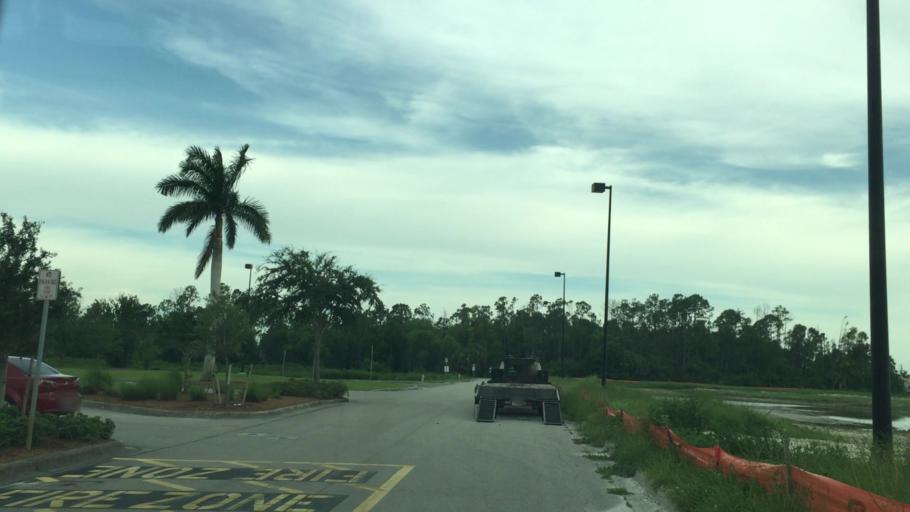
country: US
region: Florida
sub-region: Lee County
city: Fort Myers
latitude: 26.6034
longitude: -81.8100
